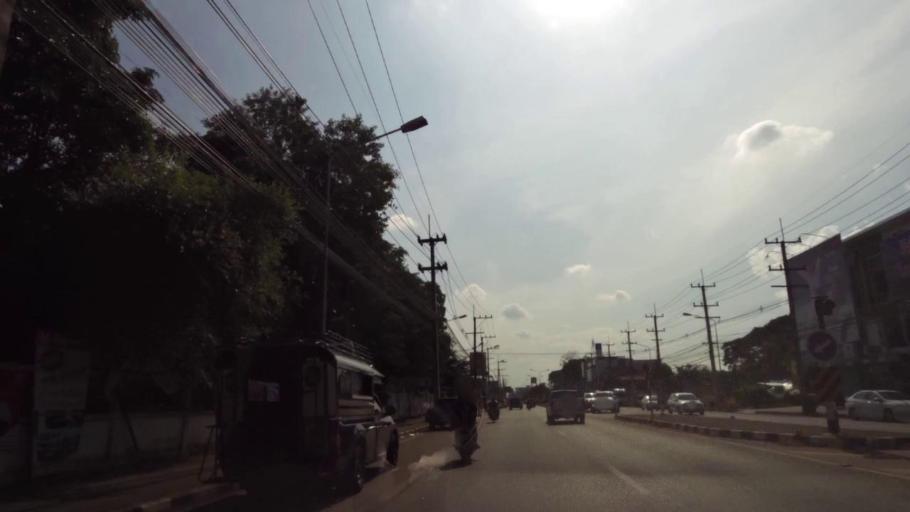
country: TH
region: Phrae
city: Phrae
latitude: 18.1296
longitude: 100.1441
